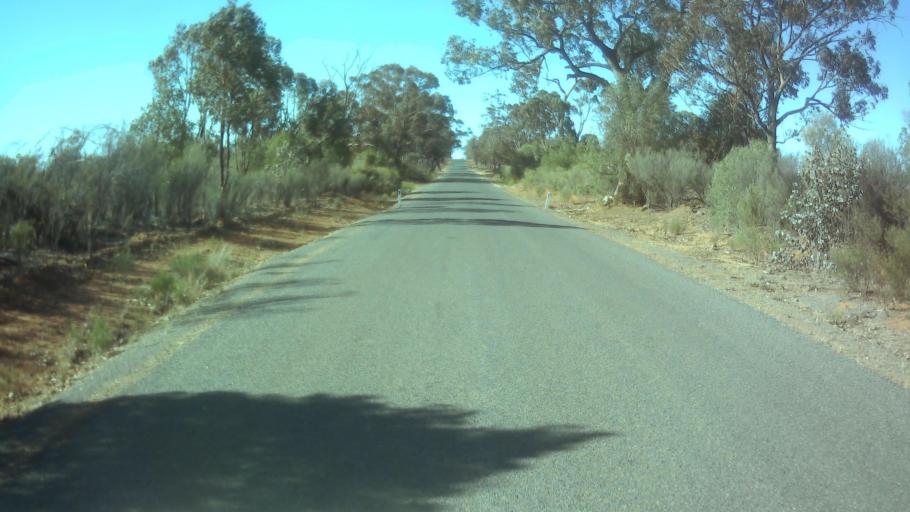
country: AU
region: New South Wales
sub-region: Forbes
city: Forbes
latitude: -33.7089
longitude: 147.8050
